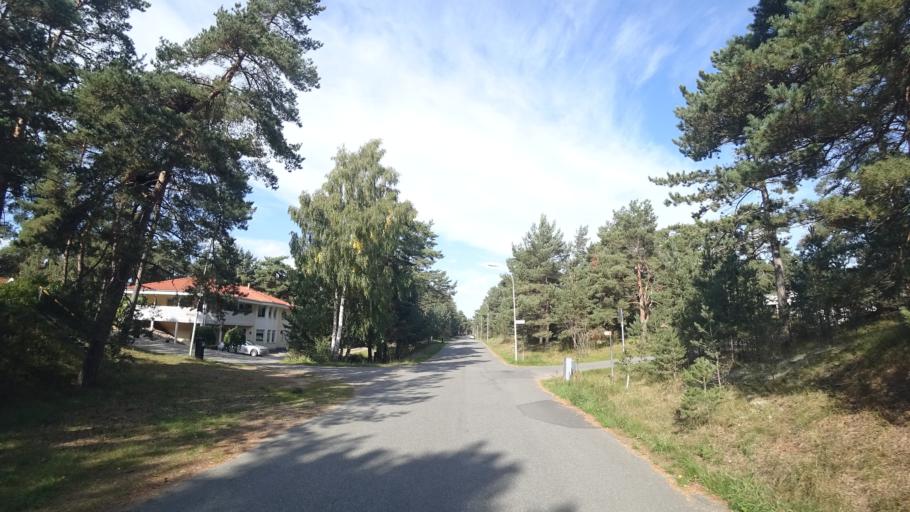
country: SE
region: Skane
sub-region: Kristianstads Kommun
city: Ahus
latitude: 55.9106
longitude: 14.2886
